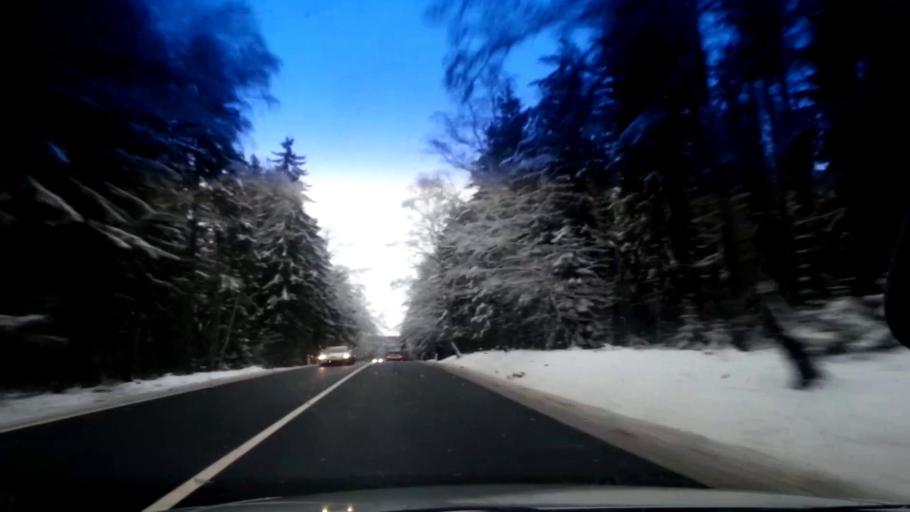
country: CZ
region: Karlovarsky
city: Hazlov
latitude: 50.1777
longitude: 12.2515
